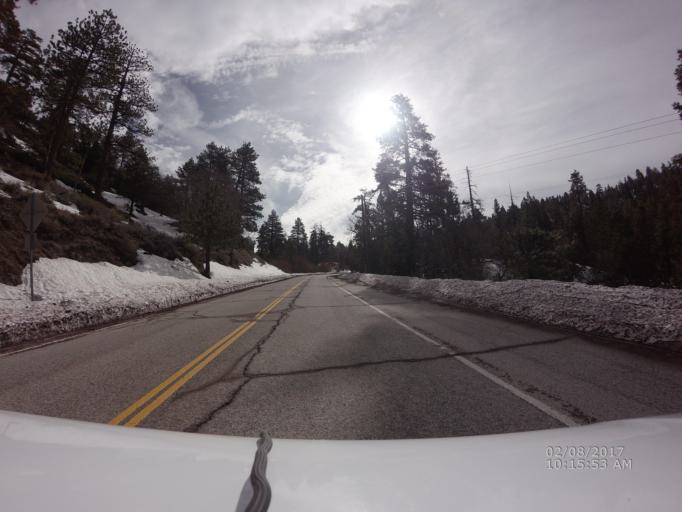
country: US
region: California
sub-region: San Bernardino County
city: Wrightwood
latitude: 34.3816
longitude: -117.6957
